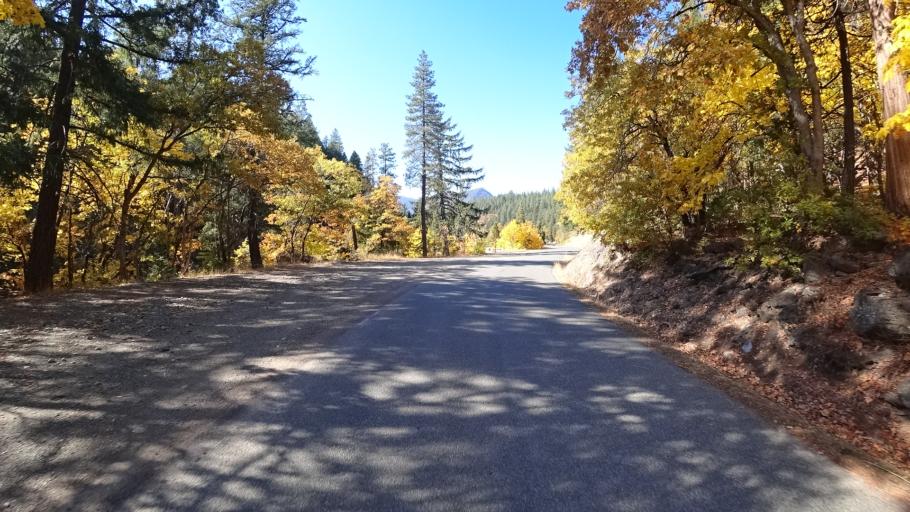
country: US
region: California
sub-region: Siskiyou County
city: Happy Camp
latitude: 41.6356
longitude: -123.0741
